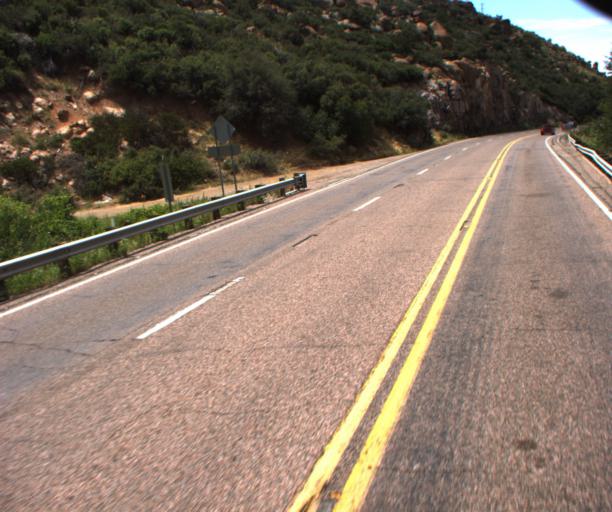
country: US
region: Arizona
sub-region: Pinal County
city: Superior
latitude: 33.3407
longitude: -111.0157
